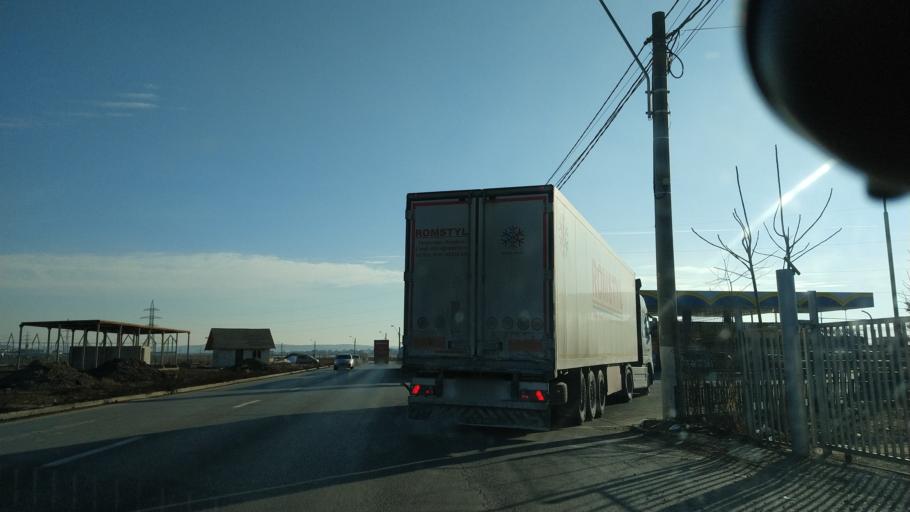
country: RO
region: Neamt
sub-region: Municipiul Roman
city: Roman
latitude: 46.9253
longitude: 26.9093
